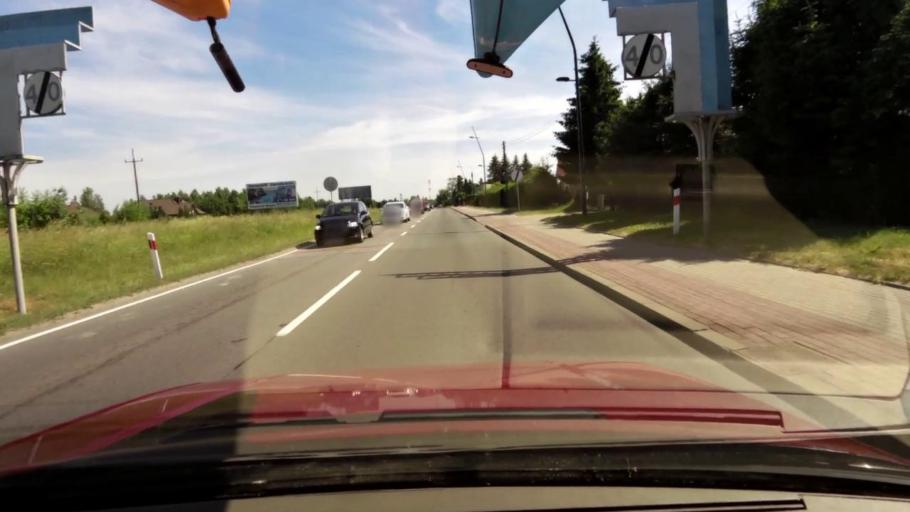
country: PL
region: Pomeranian Voivodeship
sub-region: Powiat slupski
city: Kobylnica
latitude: 54.4367
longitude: 16.9979
